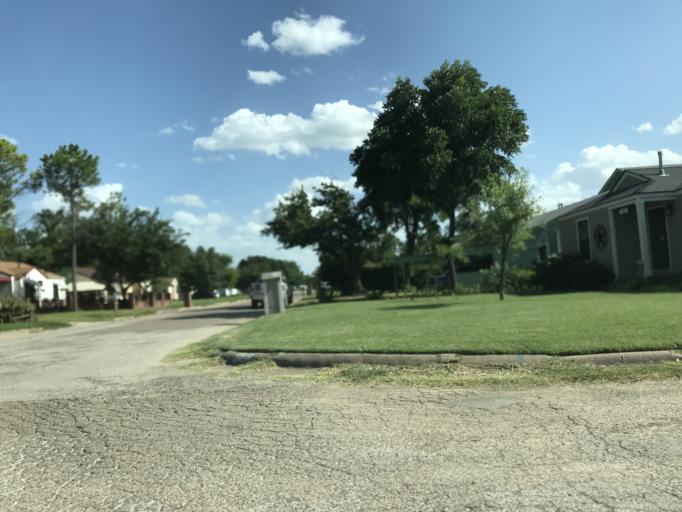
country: US
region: Texas
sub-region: Taylor County
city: Abilene
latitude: 32.4297
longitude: -99.7584
